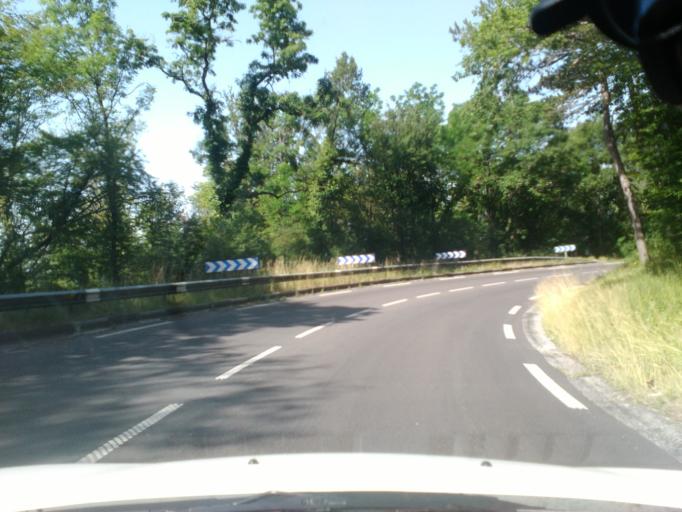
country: FR
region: Lorraine
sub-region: Departement des Vosges
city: Neufchateau
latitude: 48.3507
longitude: 5.7162
